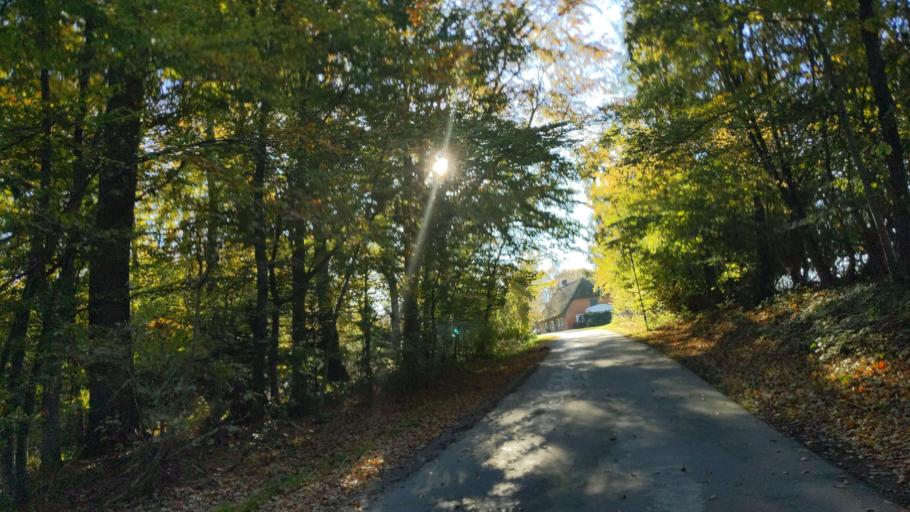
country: DE
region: Schleswig-Holstein
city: Gross Gronau
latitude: 53.7897
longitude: 10.7500
